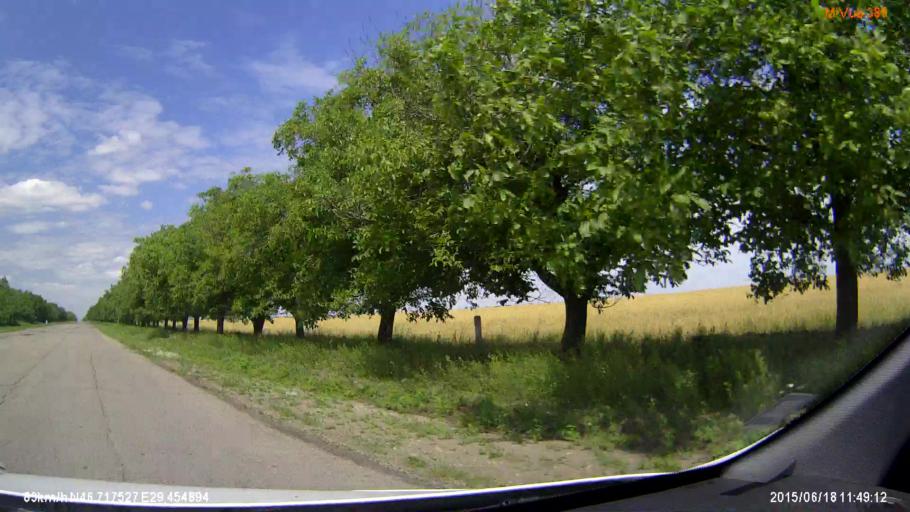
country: MD
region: Causeni
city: Causeni
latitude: 46.7171
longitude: 29.4549
